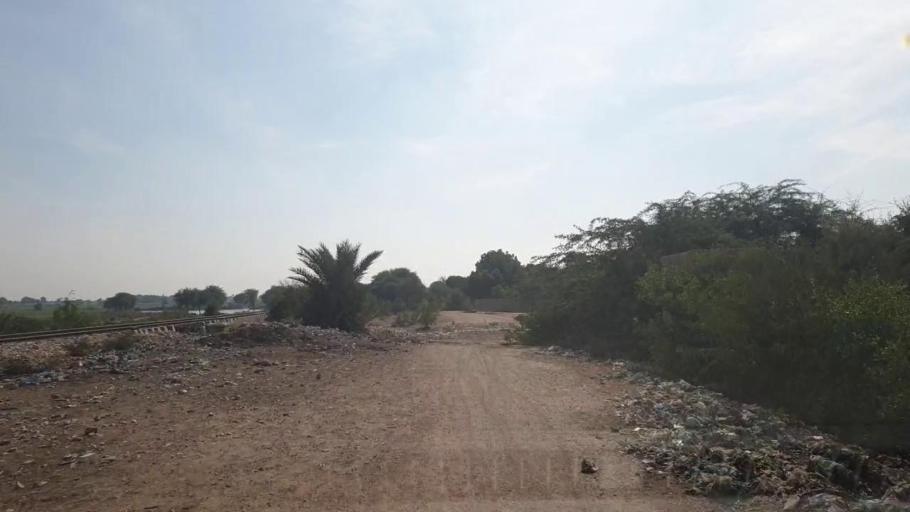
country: PK
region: Sindh
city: Hala
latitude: 25.7431
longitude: 68.2946
